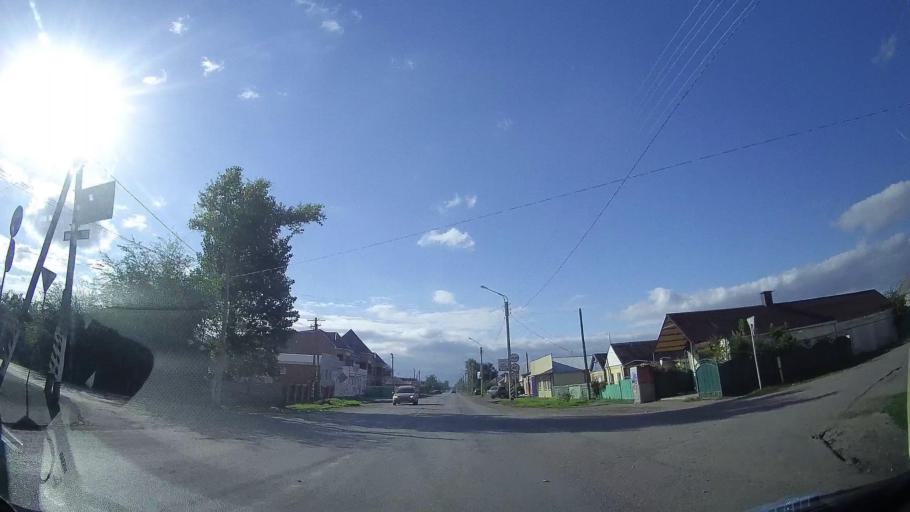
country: RU
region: Rostov
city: Tselina
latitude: 46.5304
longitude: 41.0262
